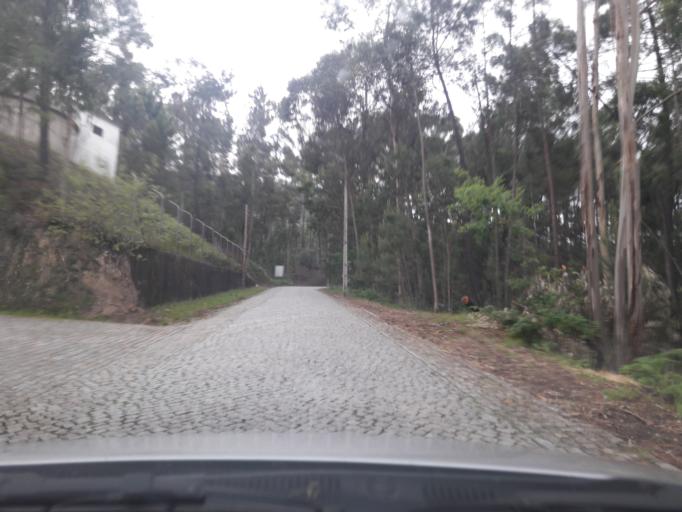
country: PT
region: Porto
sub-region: Amarante
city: Teloes
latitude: 41.3396
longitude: -8.0698
